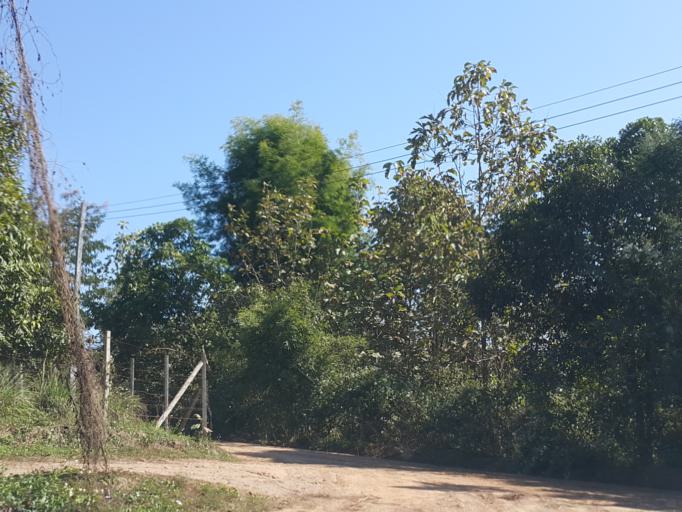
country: TH
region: Chiang Mai
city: Mae Taeng
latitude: 18.9512
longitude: 98.9041
